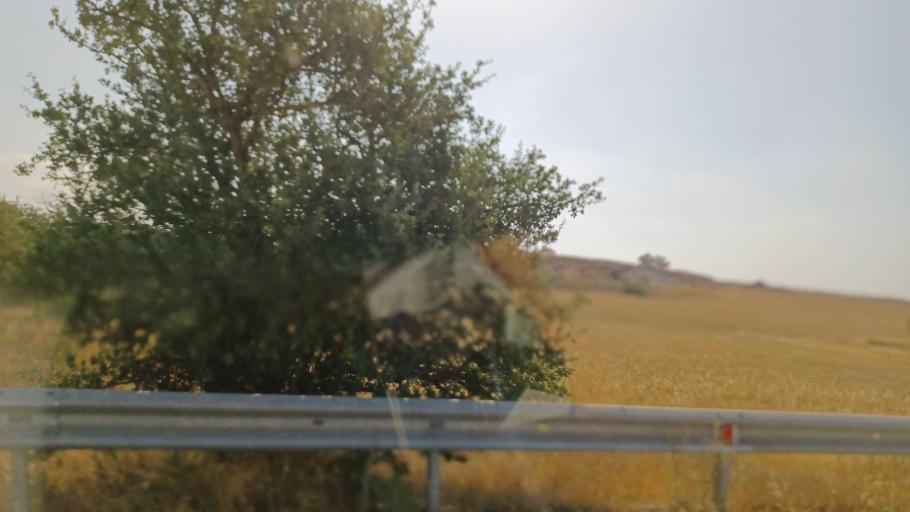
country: CY
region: Ammochostos
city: Frenaros
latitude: 35.0503
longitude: 33.8872
